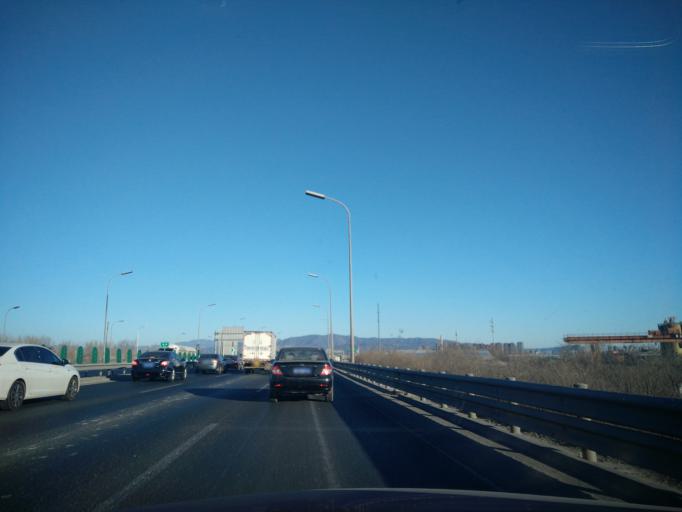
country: CN
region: Beijing
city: Lugu
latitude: 39.8698
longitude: 116.2042
